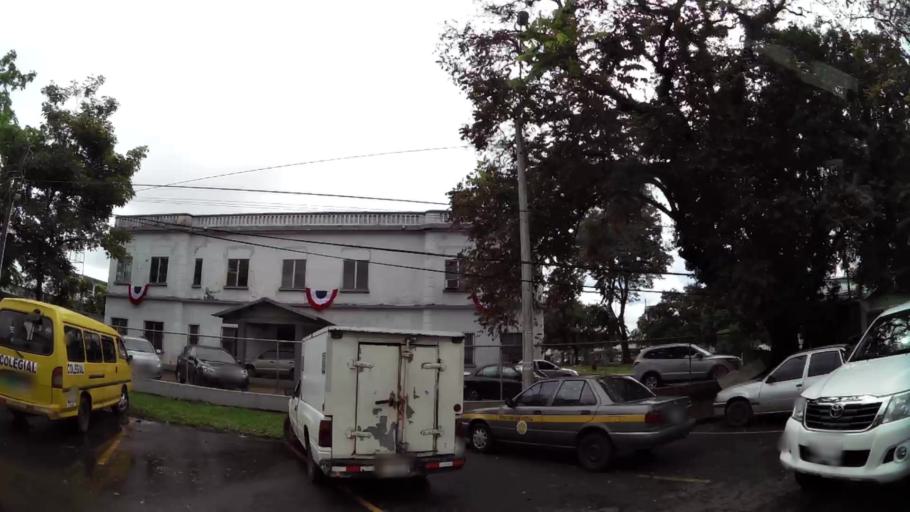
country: PA
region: Chiriqui
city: David
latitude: 8.4290
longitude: -82.4301
